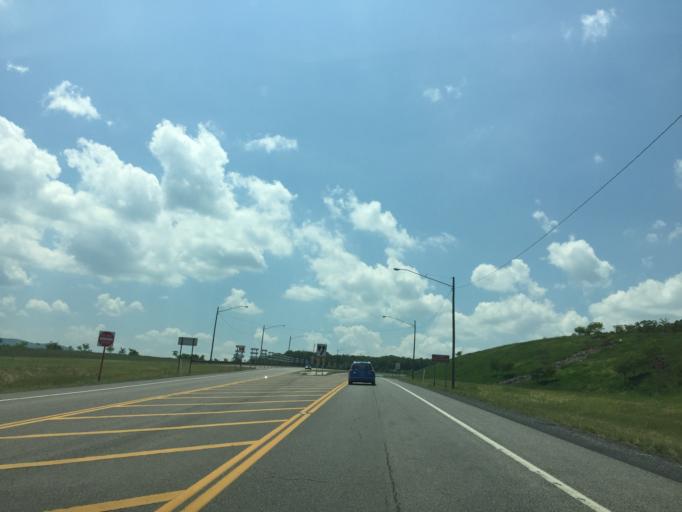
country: US
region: Virginia
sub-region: Shenandoah County
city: Woodstock
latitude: 39.0735
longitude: -78.6282
